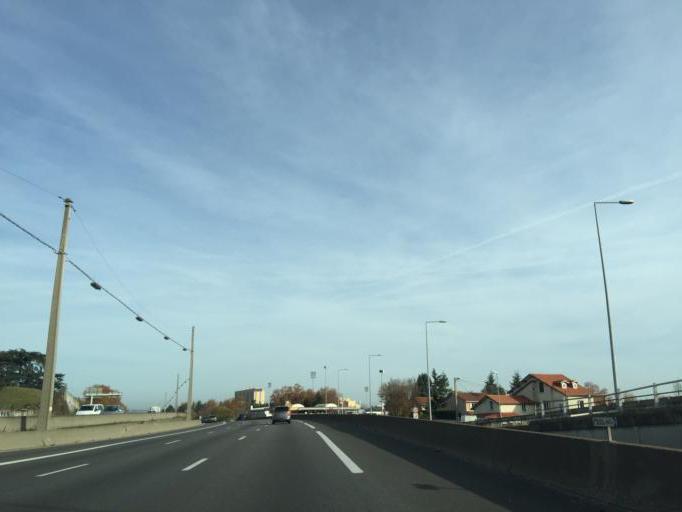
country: FR
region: Rhone-Alpes
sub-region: Departement du Rhone
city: Bron
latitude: 45.7375
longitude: 4.9038
